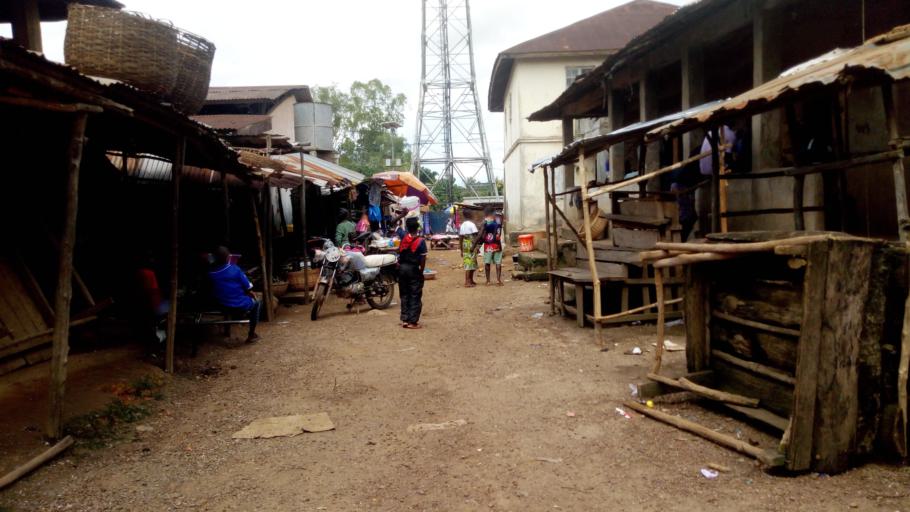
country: SL
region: Northern Province
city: Magburaka
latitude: 8.7228
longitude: -11.9513
